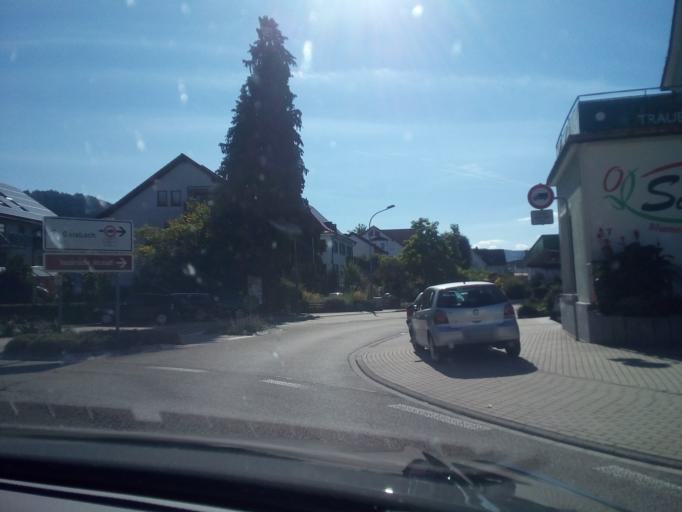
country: DE
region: Baden-Wuerttemberg
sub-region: Freiburg Region
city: Oberkirch
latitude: 48.5381
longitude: 8.0731
